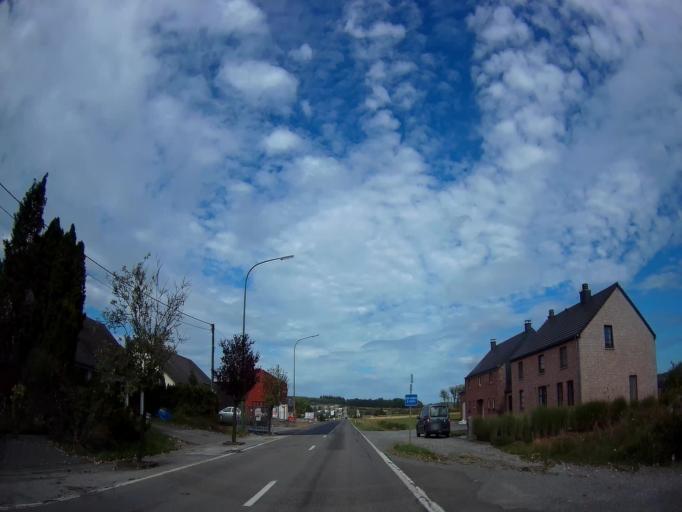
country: BE
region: Wallonia
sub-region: Province du Luxembourg
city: Hotton
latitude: 50.2748
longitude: 5.4522
